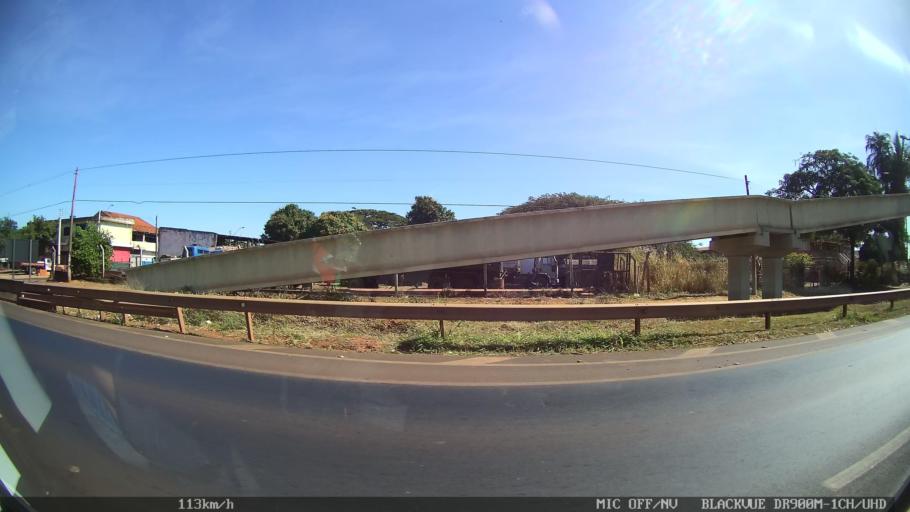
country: BR
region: Sao Paulo
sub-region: Barretos
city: Barretos
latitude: -20.5496
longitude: -48.5924
